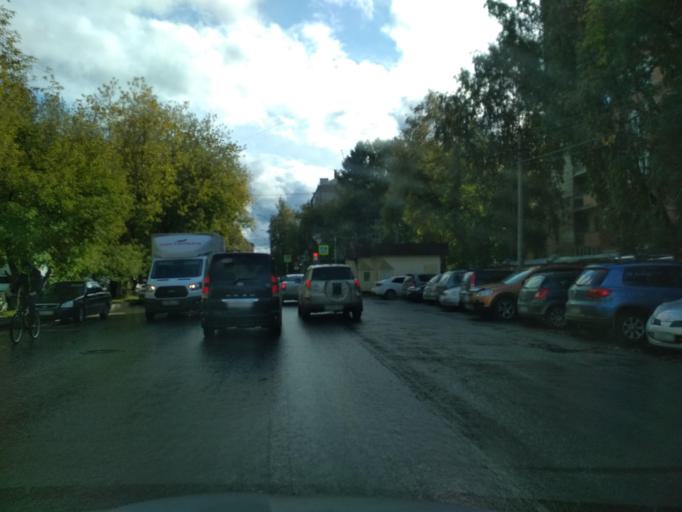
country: RU
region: Tomsk
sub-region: Tomskiy Rayon
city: Tomsk
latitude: 56.4645
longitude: 84.9756
